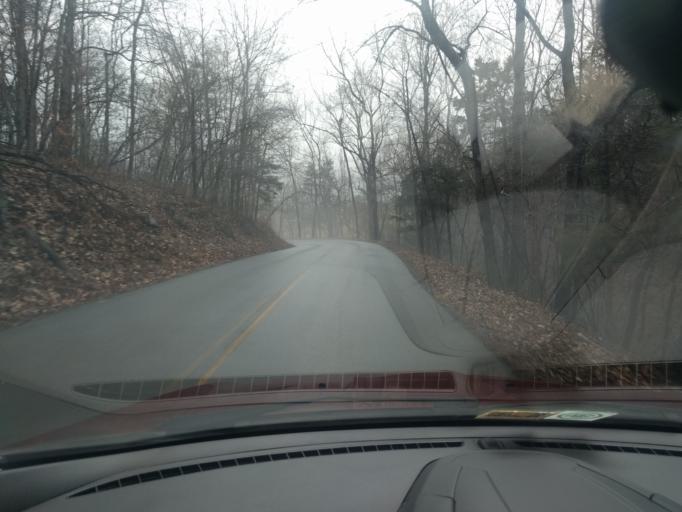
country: US
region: Virginia
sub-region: Botetourt County
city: Fincastle
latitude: 37.5574
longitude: -79.8764
